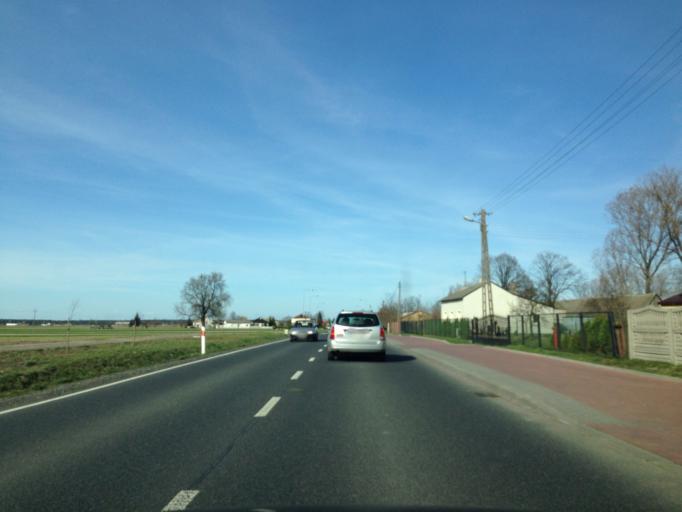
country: PL
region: Lodz Voivodeship
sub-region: Powiat poddebicki
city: Wartkowice
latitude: 51.9845
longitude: 19.0321
